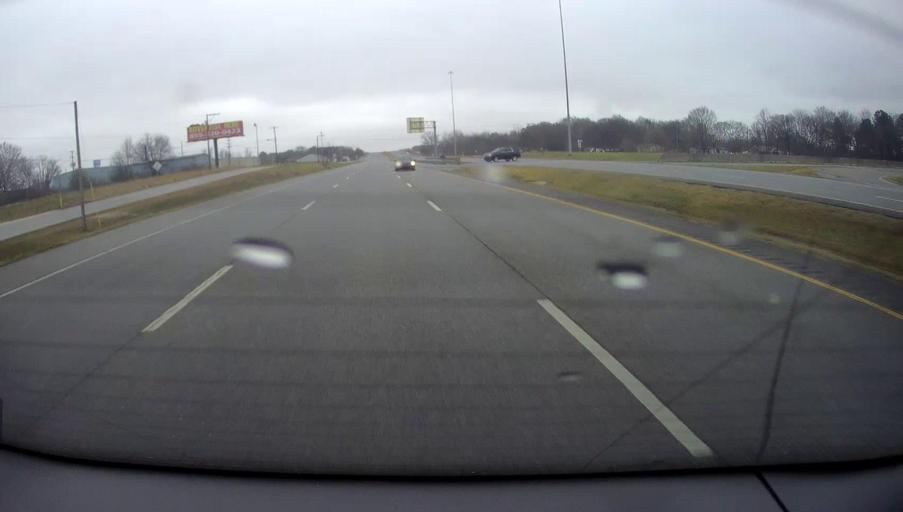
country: US
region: Alabama
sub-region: Morgan County
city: Decatur
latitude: 34.6028
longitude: -87.0314
